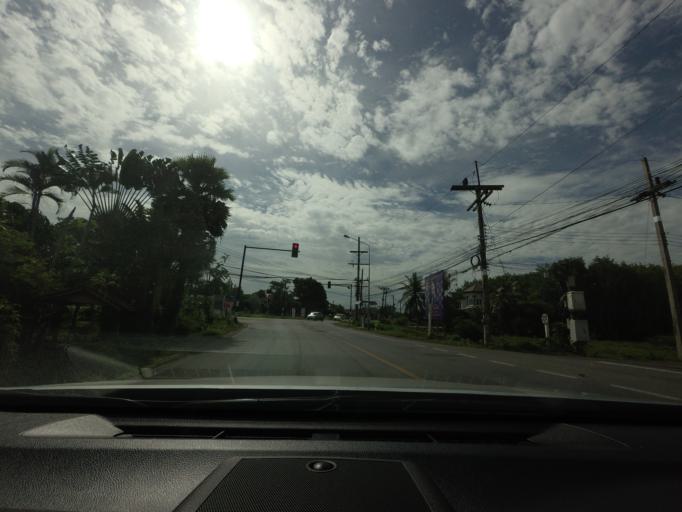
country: TH
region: Songkhla
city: Khlong Hoi Khong
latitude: 6.9102
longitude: 100.4129
